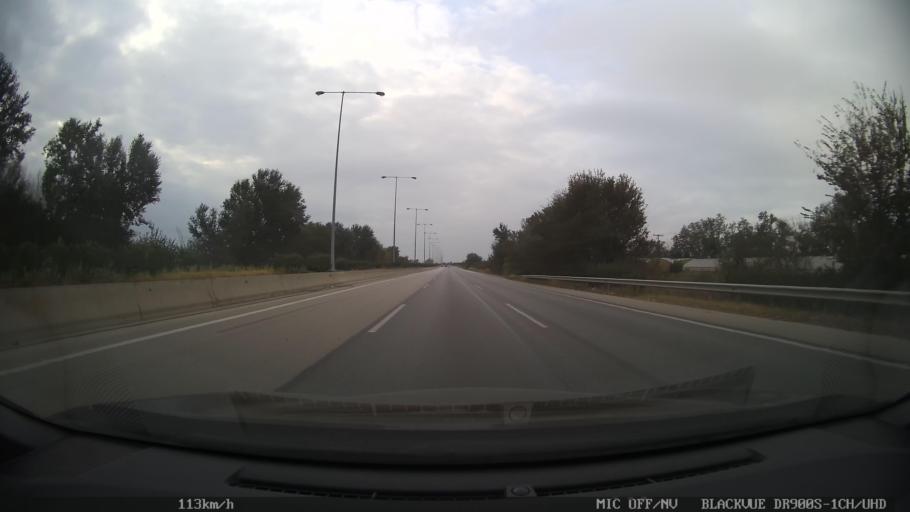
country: GR
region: Central Macedonia
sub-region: Nomos Thessalonikis
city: Nea Magnisia
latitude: 40.6832
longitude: 22.8325
